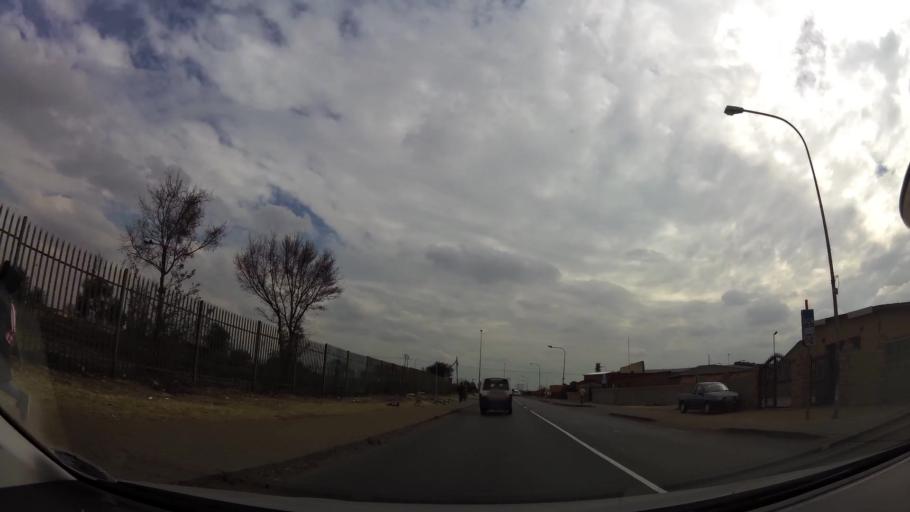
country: ZA
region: Gauteng
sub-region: City of Johannesburg Metropolitan Municipality
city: Soweto
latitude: -26.2728
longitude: 27.8621
